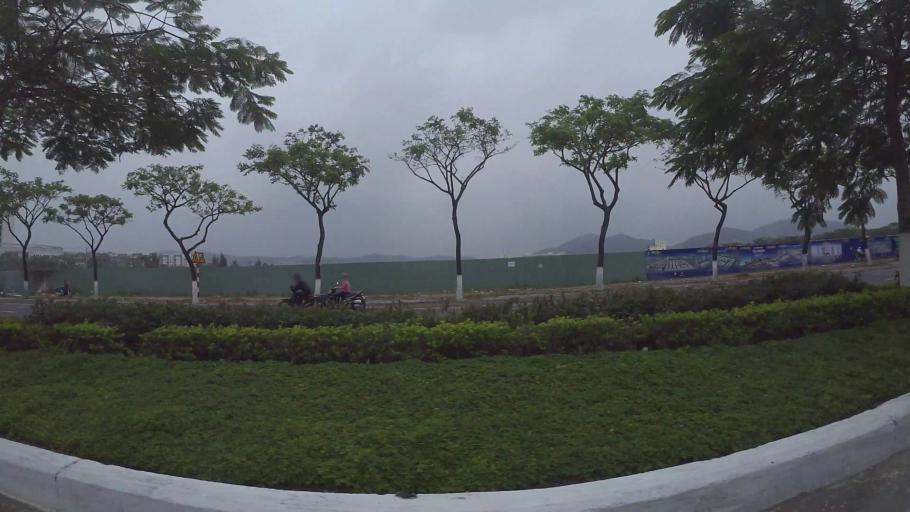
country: VN
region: Da Nang
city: Lien Chieu
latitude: 16.0727
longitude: 108.1626
